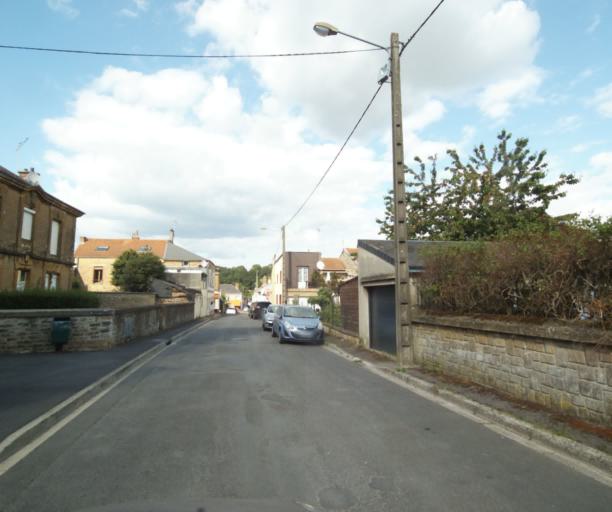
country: FR
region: Champagne-Ardenne
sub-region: Departement des Ardennes
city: Montcy-Notre-Dame
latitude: 49.7765
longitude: 4.7337
